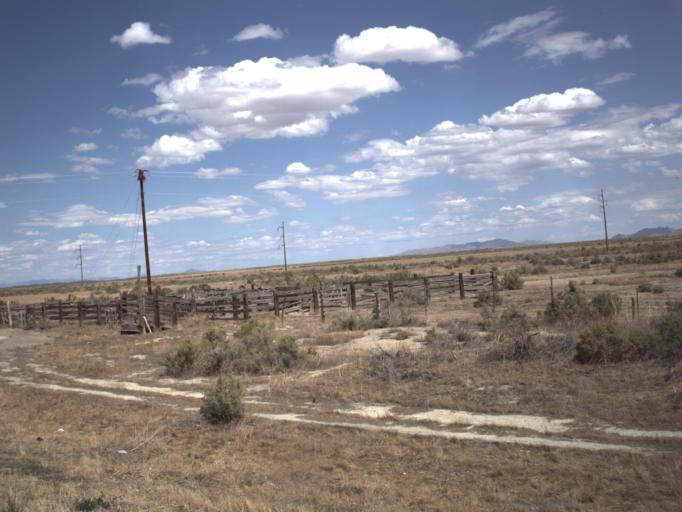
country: US
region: Utah
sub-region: Millard County
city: Delta
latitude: 39.2863
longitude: -112.4635
